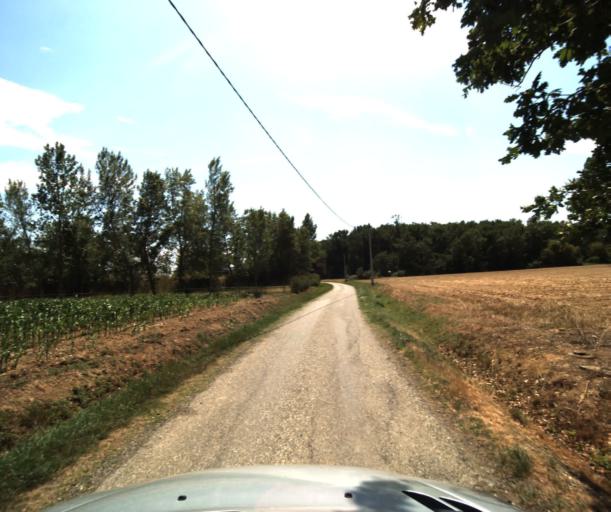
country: FR
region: Midi-Pyrenees
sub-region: Departement de la Haute-Garonne
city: Labastidette
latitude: 43.4647
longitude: 1.2344
